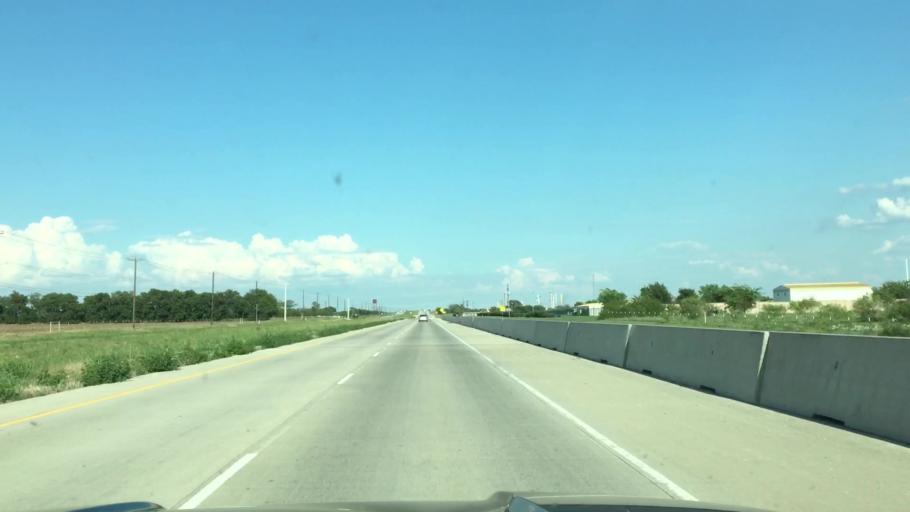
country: US
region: Texas
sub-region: Tarrant County
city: Haslet
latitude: 33.0353
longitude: -97.3569
